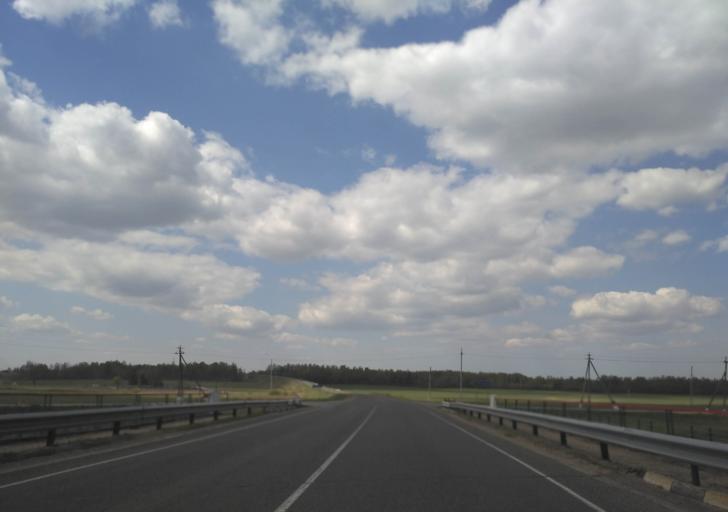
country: BY
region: Minsk
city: Vilyeyka
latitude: 54.5213
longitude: 26.9692
